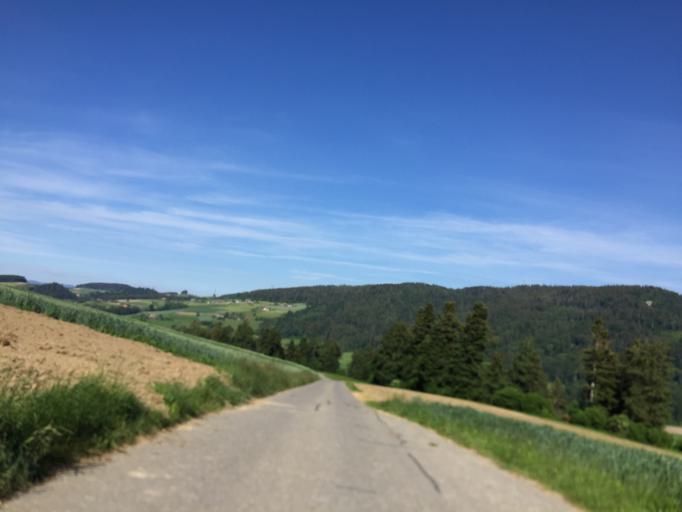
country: CH
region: Lucerne
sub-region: Entlebuch District
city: Oberdiessbach
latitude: 46.8578
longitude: 7.6120
